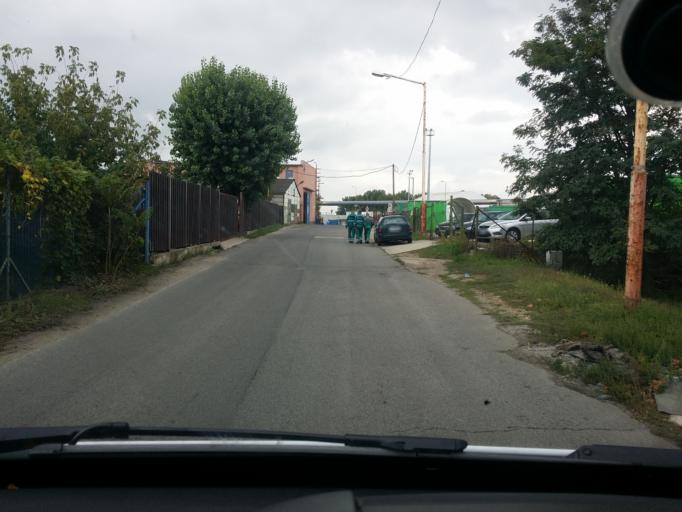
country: HU
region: Budapest
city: Budapest XXII. keruelet
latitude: 47.4220
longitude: 19.0519
